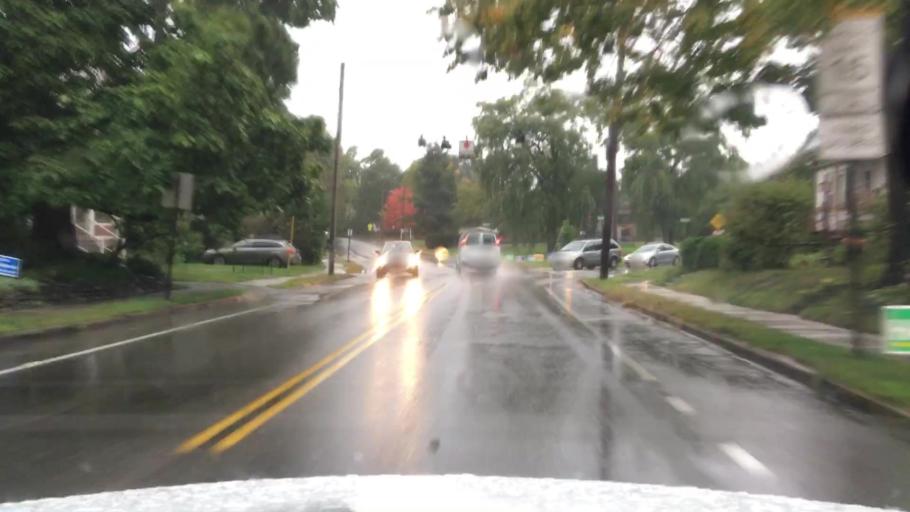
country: US
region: Maine
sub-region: Cumberland County
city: Portland
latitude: 43.6671
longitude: -70.2840
